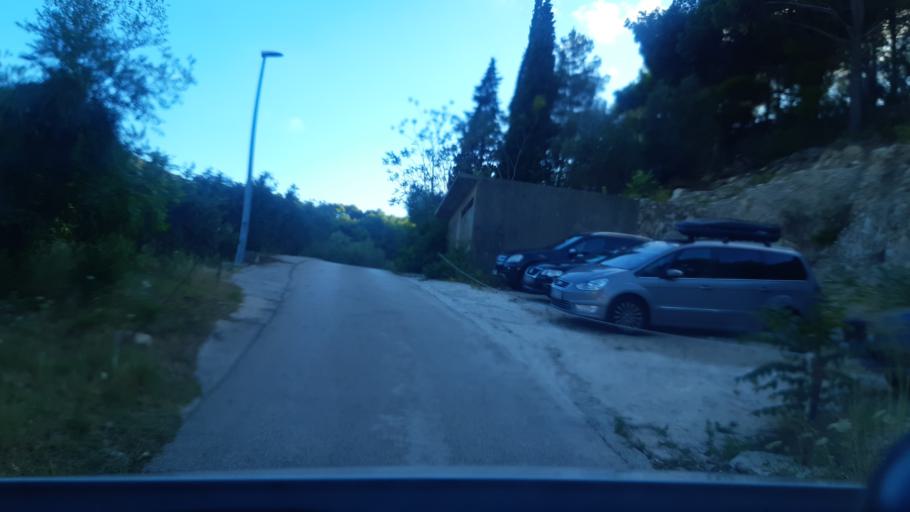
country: HR
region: Dubrovacko-Neretvanska
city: Blato
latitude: 42.8895
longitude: 17.4532
